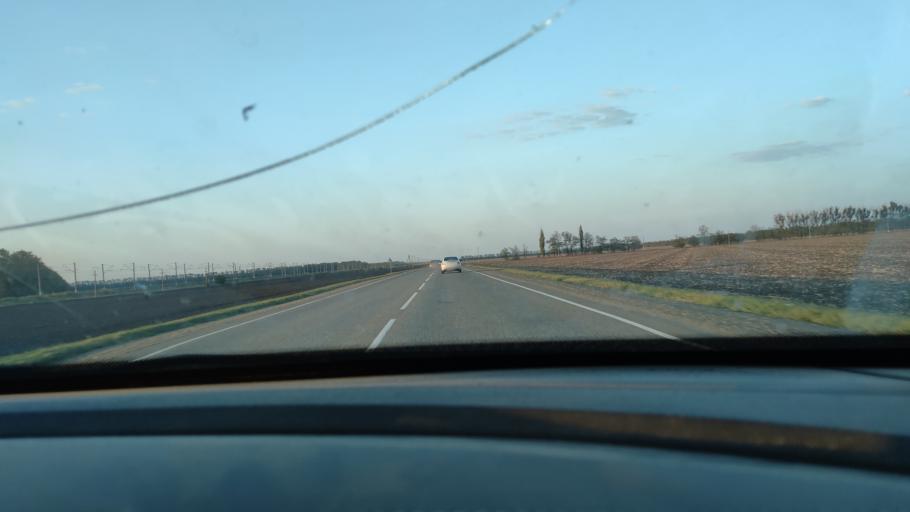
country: RU
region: Krasnodarskiy
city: Novominskaya
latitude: 46.3567
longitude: 38.9652
